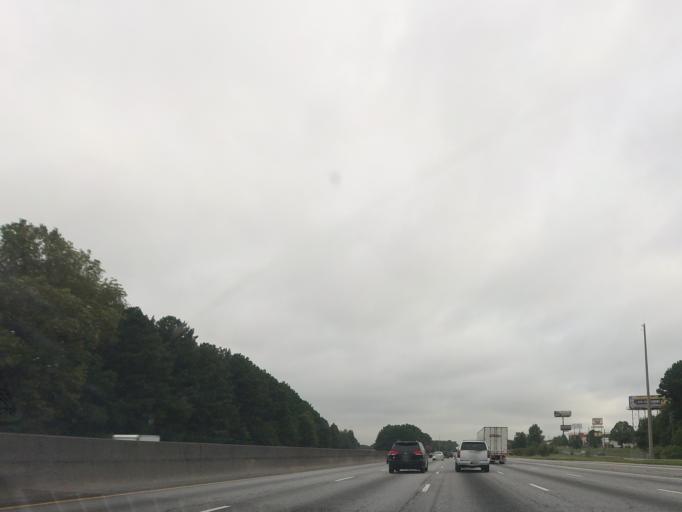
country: US
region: Georgia
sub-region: Clayton County
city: Forest Park
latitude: 33.6225
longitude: -84.3996
